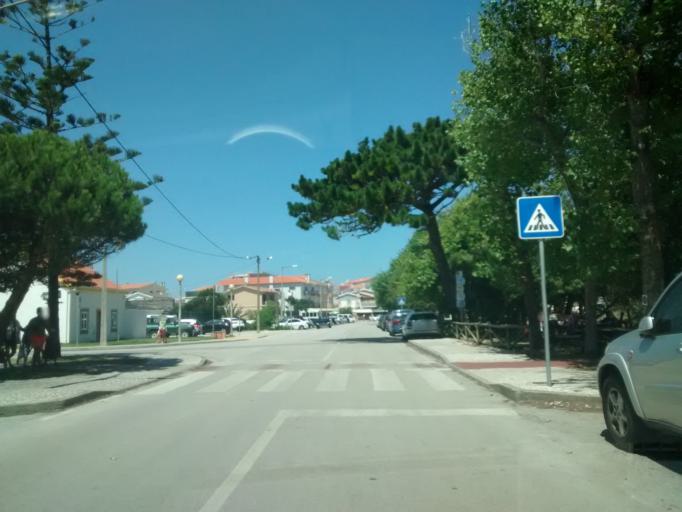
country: PT
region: Coimbra
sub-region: Mira
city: Mira
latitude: 40.4503
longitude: -8.8014
